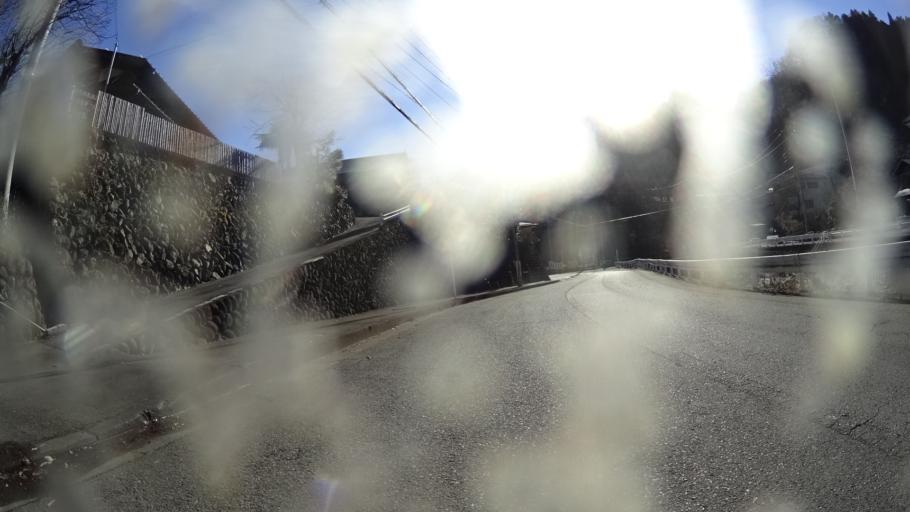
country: JP
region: Yamanashi
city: Uenohara
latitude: 35.6344
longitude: 139.1415
